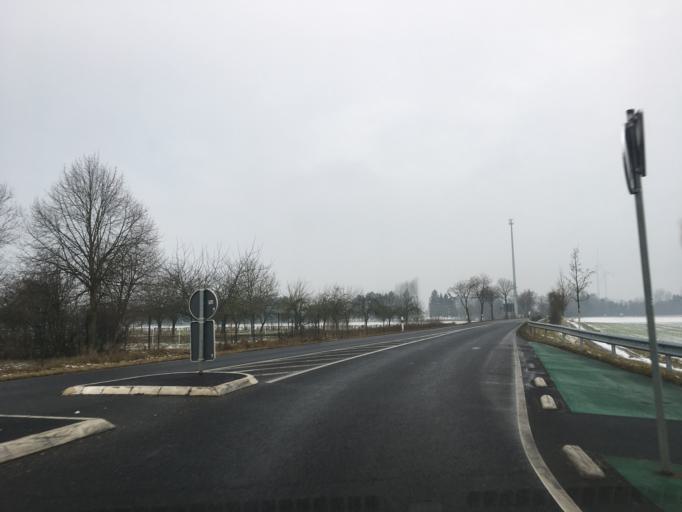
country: DE
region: North Rhine-Westphalia
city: Wegberg
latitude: 51.1166
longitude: 6.2453
